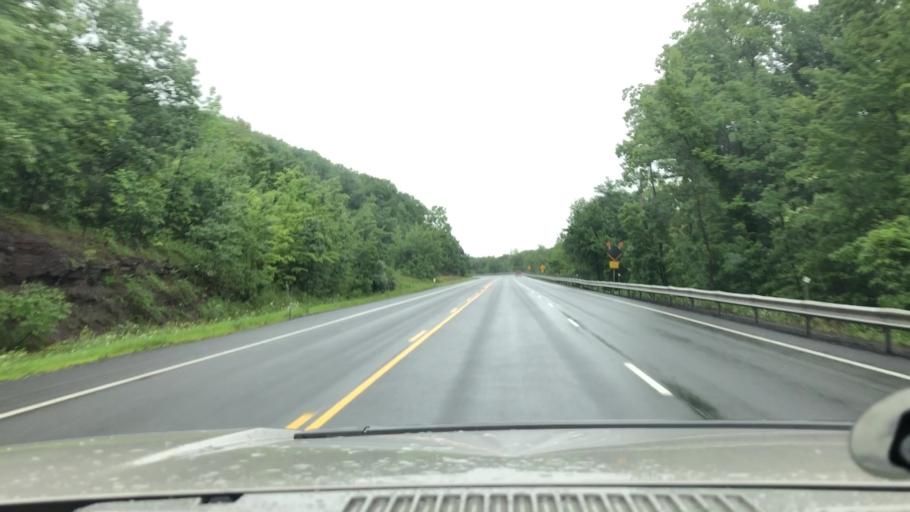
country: US
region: New York
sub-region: Greene County
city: Cairo
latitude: 42.3343
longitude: -74.1151
